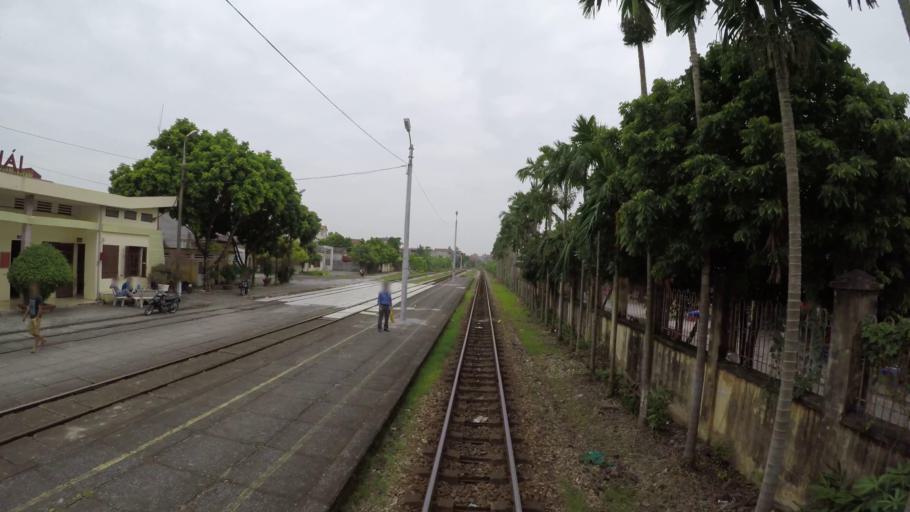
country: VN
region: Hai Duong
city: Phu Thai
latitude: 20.9729
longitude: 106.4869
